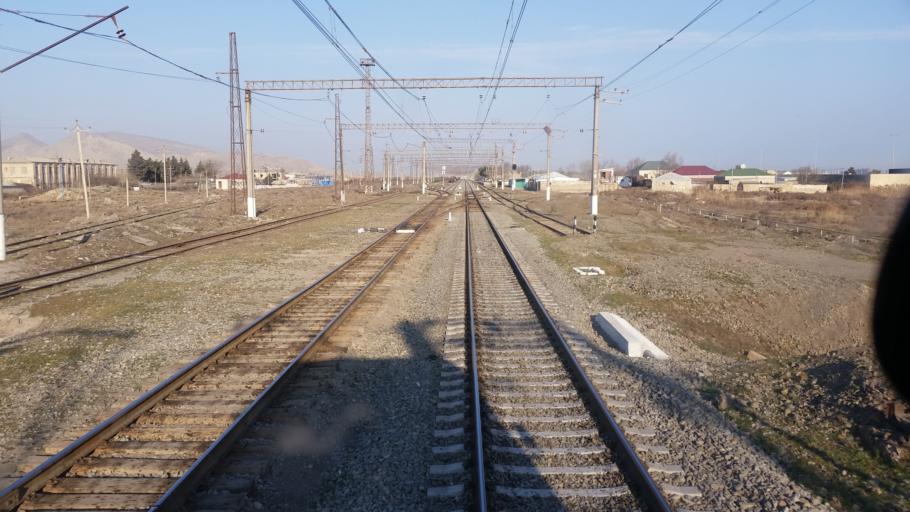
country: AZ
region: Baki
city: Korgoz
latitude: 40.2384
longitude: 49.5900
